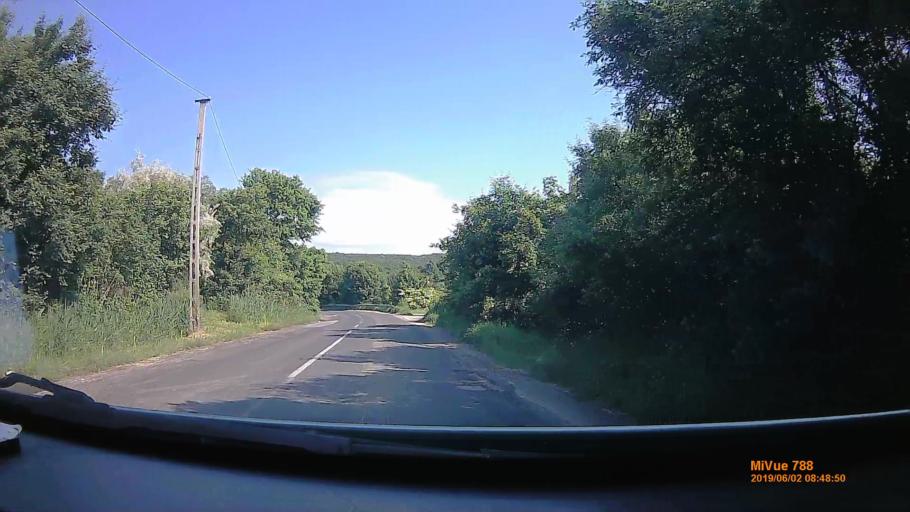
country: HU
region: Borsod-Abauj-Zemplen
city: Sajobabony
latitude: 48.1396
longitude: 20.7029
